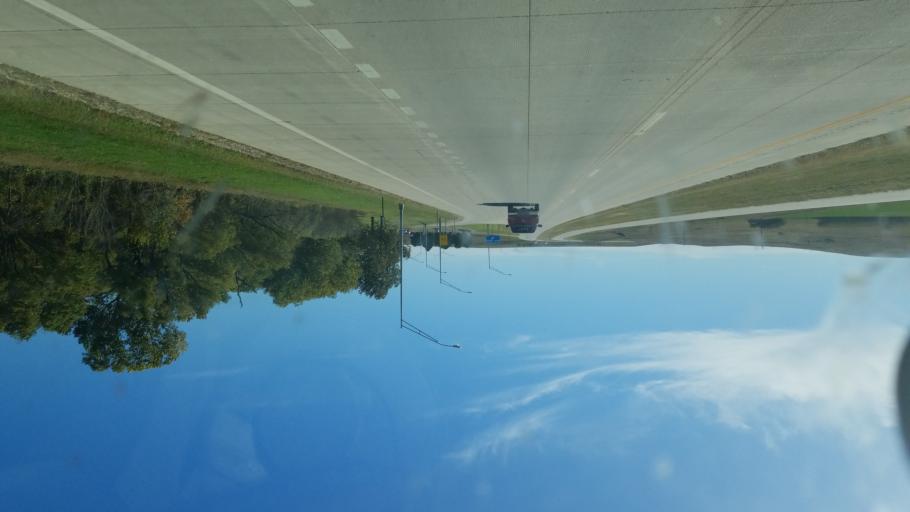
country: US
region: Kansas
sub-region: Ellsworth County
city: Ellsworth
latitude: 38.8567
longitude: -98.1299
